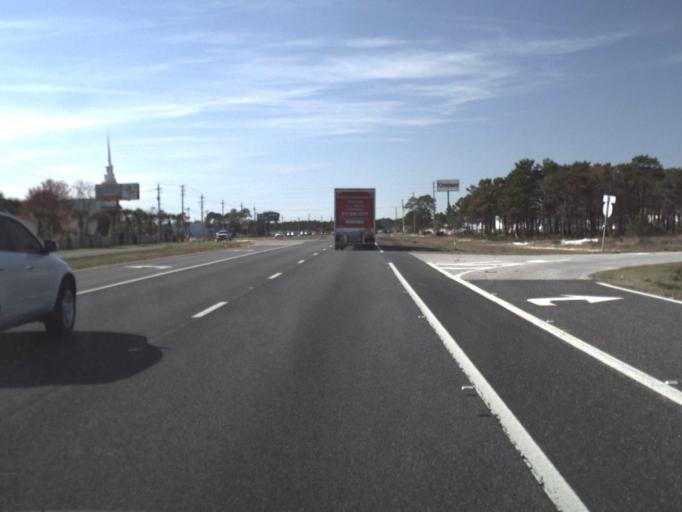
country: US
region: Florida
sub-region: Bay County
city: Laguna Beach
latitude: 30.2339
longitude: -85.8982
